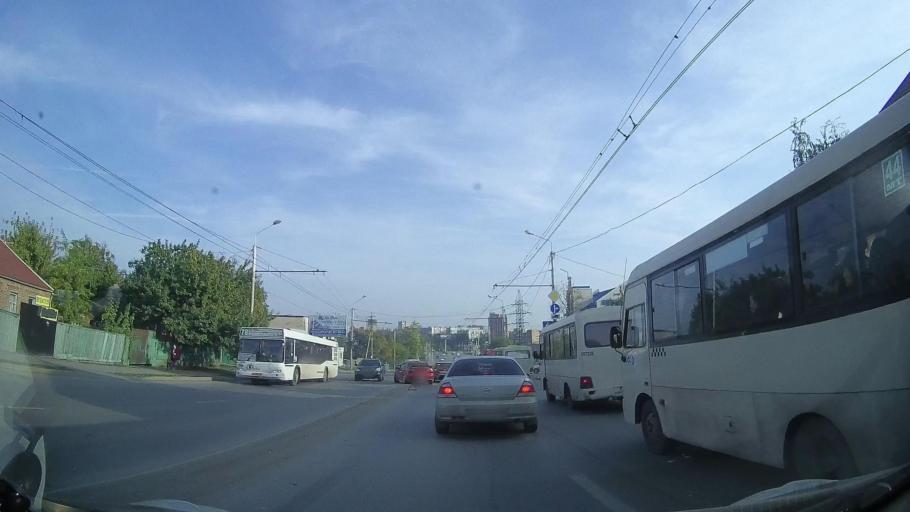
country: RU
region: Rostov
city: Severnyy
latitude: 47.2957
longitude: 39.7278
